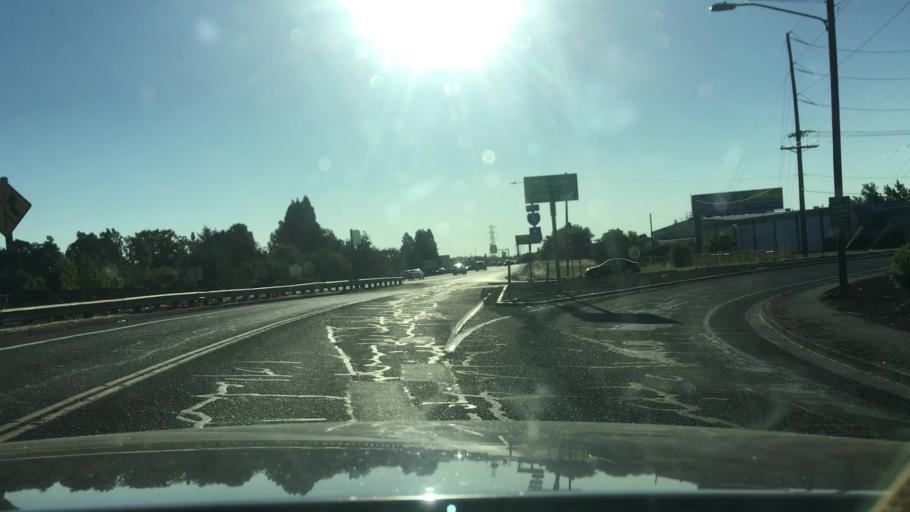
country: US
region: Oregon
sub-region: Lane County
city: Springfield
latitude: 44.0622
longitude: -123.0293
